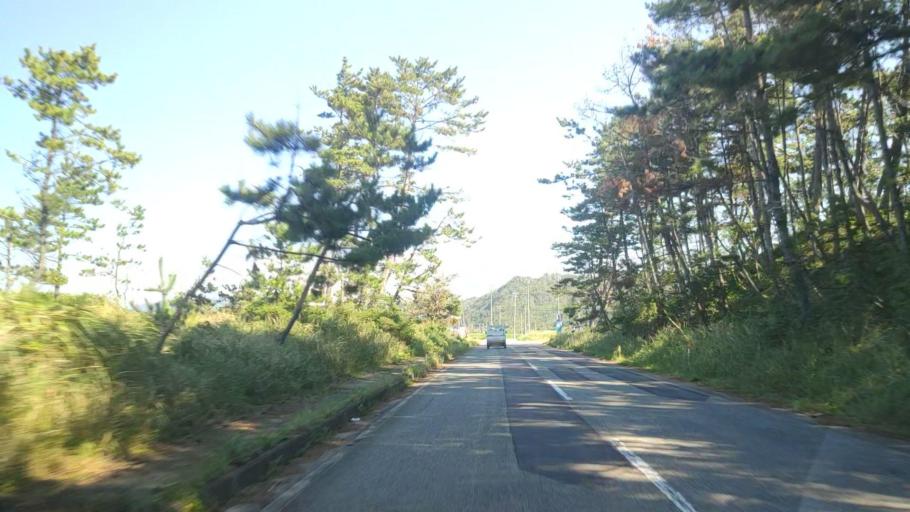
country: JP
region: Ishikawa
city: Nanao
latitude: 37.2591
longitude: 136.7240
